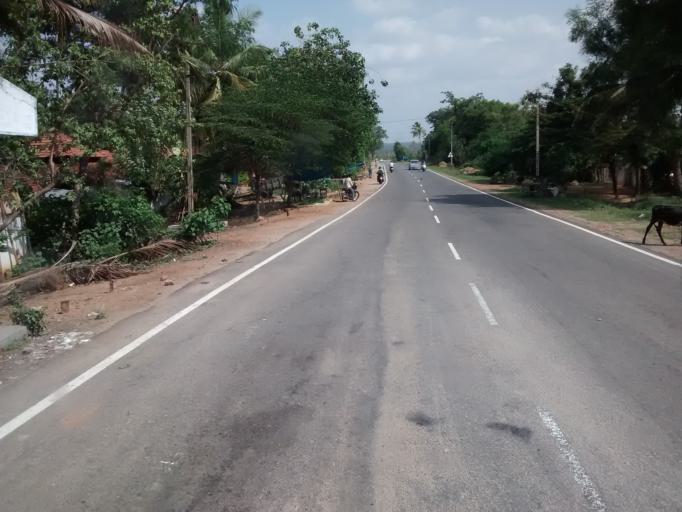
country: IN
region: Karnataka
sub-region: Mysore
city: Hunsur
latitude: 12.3915
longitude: 76.4089
